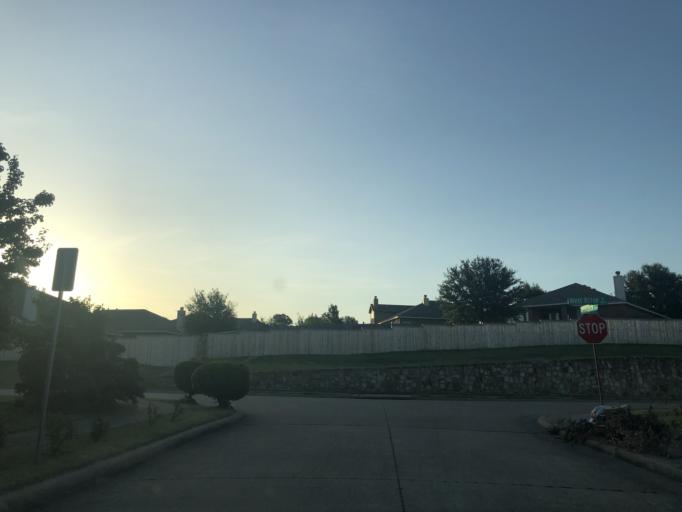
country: US
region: Texas
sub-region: Dallas County
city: Duncanville
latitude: 32.6489
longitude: -96.9523
